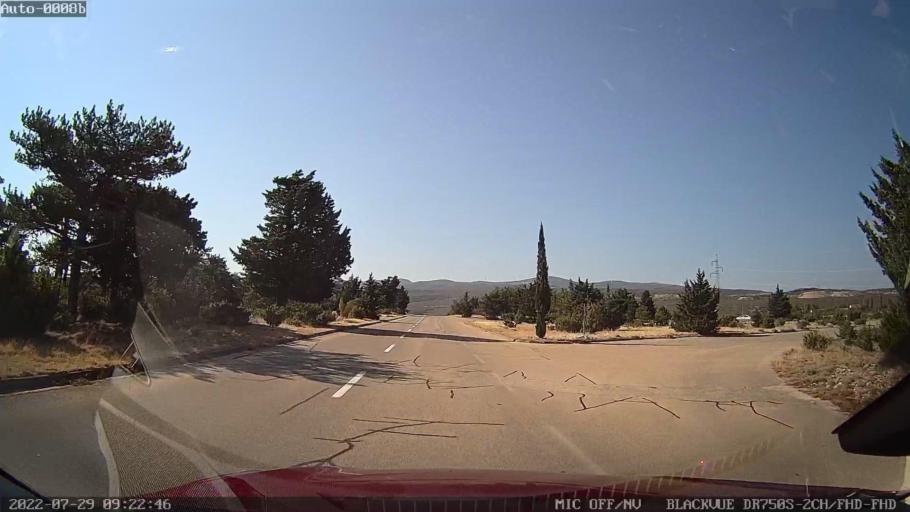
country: HR
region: Zadarska
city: Obrovac
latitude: 44.2132
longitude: 15.6679
